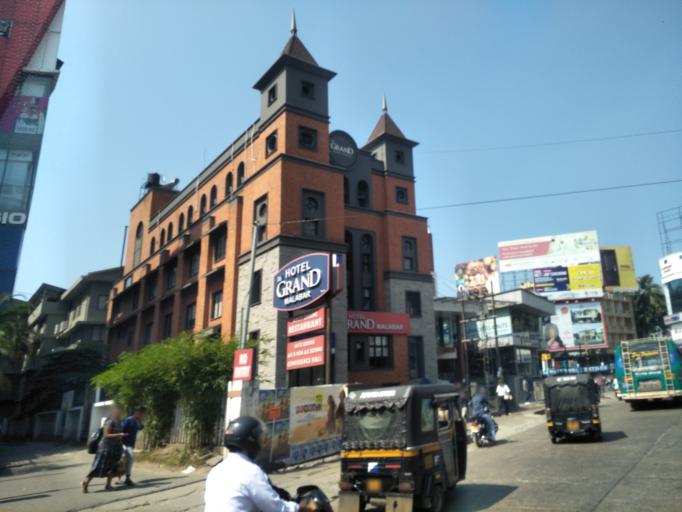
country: IN
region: Kerala
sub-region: Kozhikode
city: Kozhikode
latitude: 11.2588
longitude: 75.7860
